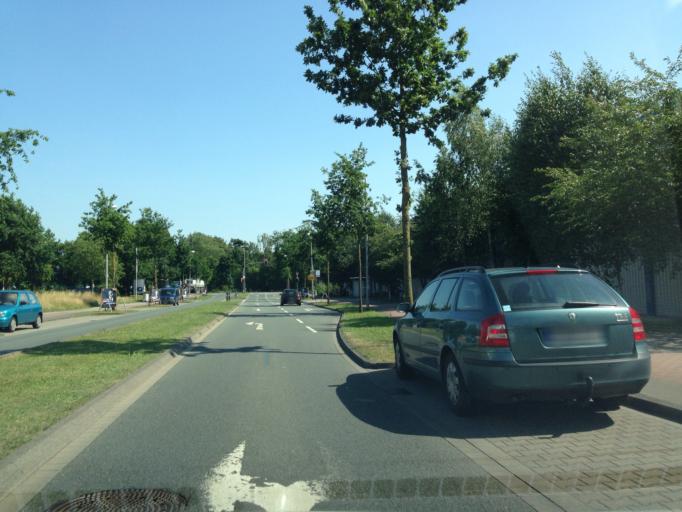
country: DE
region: North Rhine-Westphalia
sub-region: Regierungsbezirk Munster
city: Muenster
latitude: 51.9586
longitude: 7.5711
